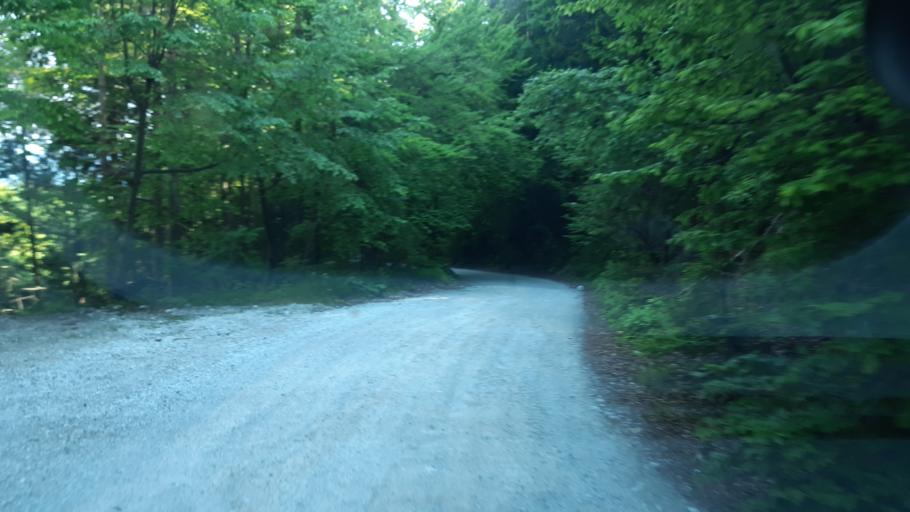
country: SI
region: Trzic
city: Bistrica pri Trzicu
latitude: 46.3673
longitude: 14.2781
